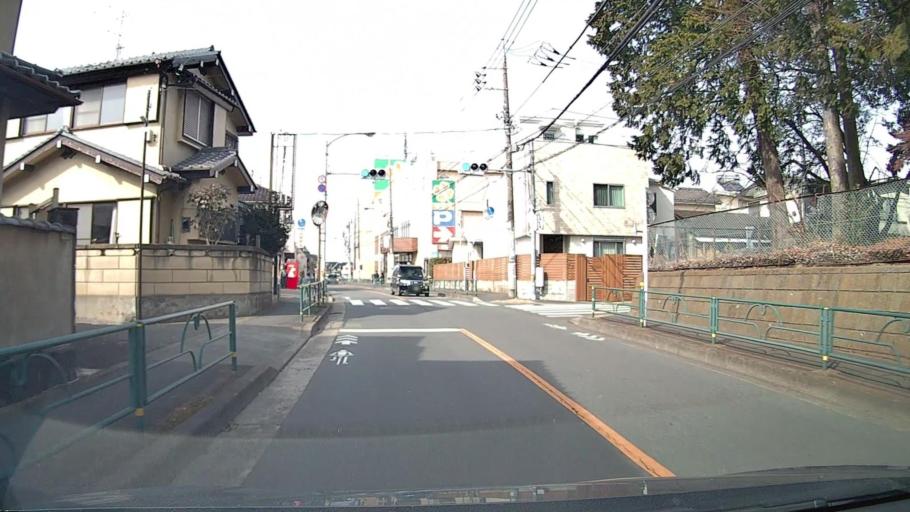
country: JP
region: Tokyo
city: Nishi-Tokyo-shi
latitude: 35.7556
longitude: 139.5798
